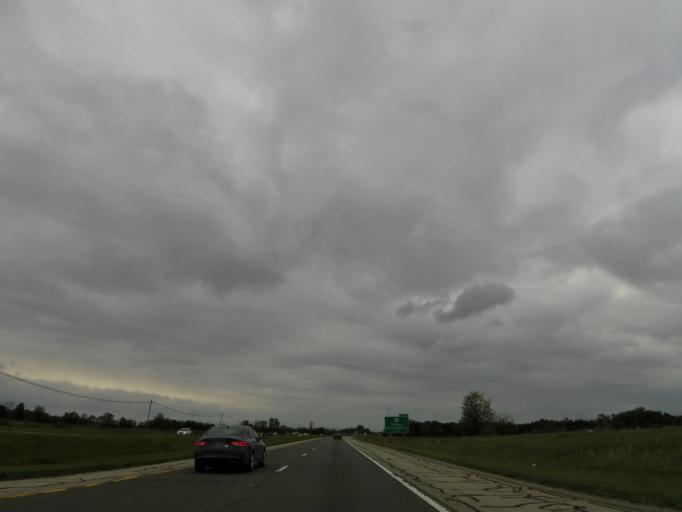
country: US
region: Ohio
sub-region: Madison County
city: Bethel
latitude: 39.6868
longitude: -83.4763
